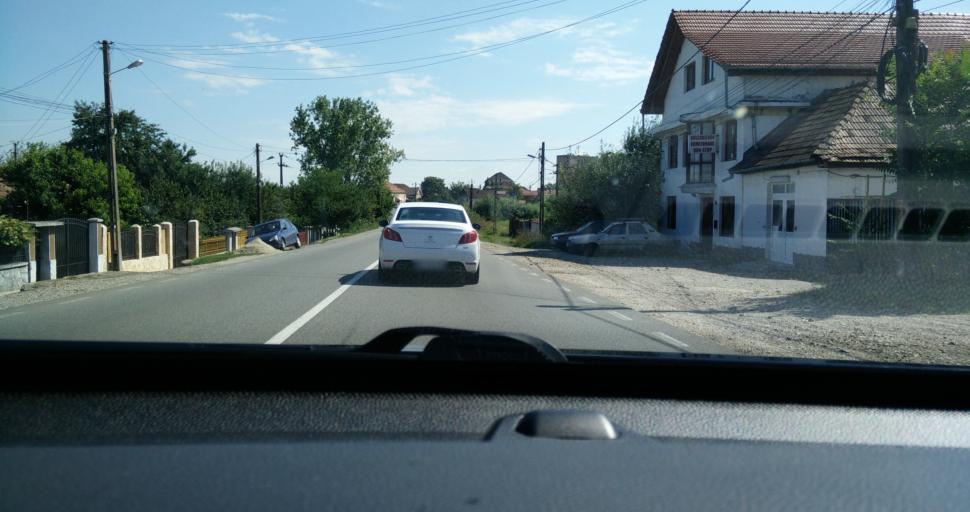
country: RO
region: Bihor
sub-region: Comuna Osorheiu
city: Alparea
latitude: 47.0398
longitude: 22.0228
